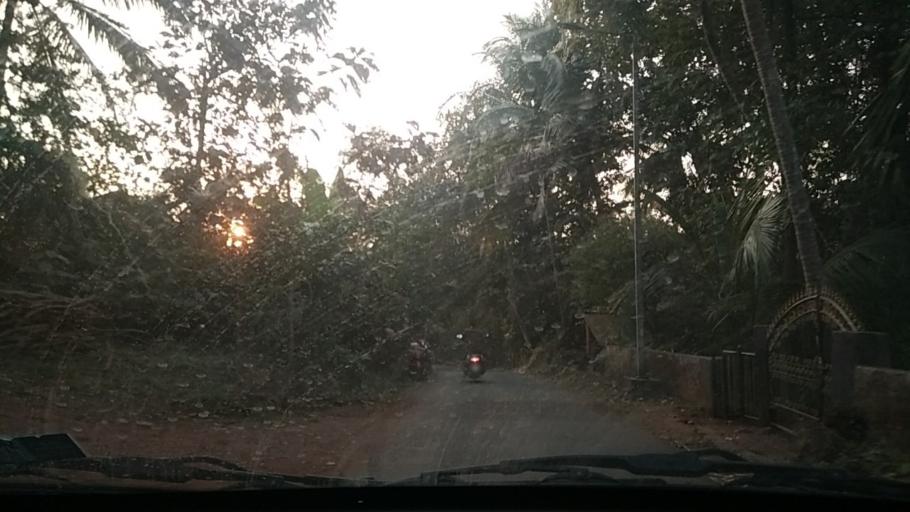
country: IN
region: Goa
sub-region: South Goa
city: Sancoale
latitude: 15.3514
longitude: 73.9396
